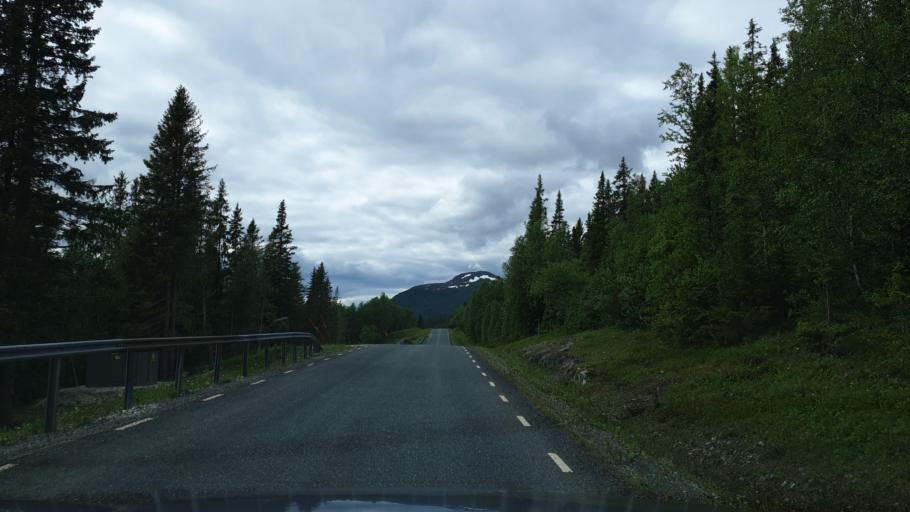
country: NO
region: Nordland
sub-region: Hattfjelldal
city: Hattfjelldal
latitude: 65.4435
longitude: 14.5410
